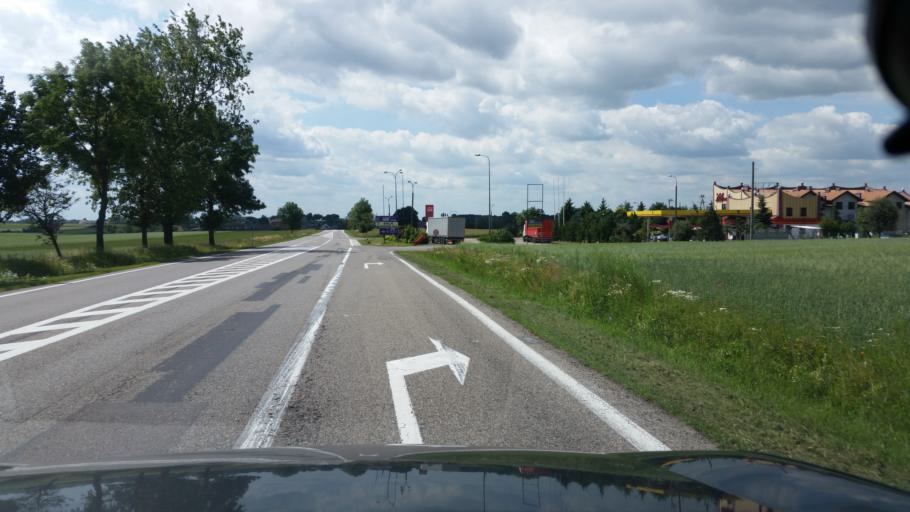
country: PL
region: Podlasie
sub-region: Powiat lomzynski
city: Piatnica
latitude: 53.2597
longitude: 22.1245
